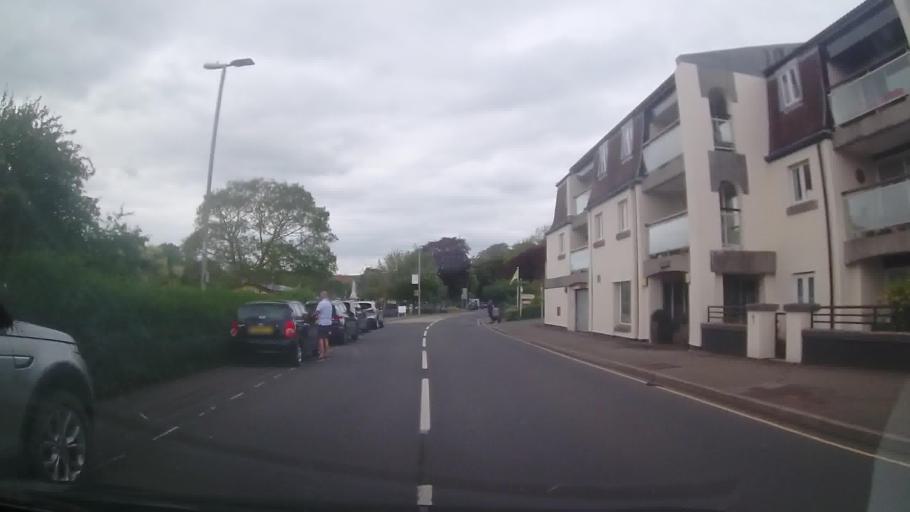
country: GB
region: England
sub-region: Devon
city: Kingsbridge
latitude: 50.2803
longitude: -3.7743
